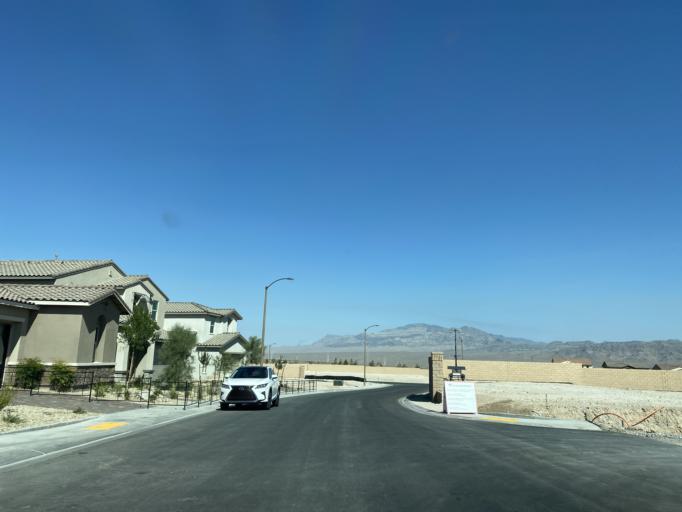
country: US
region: Nevada
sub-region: Clark County
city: Summerlin South
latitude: 36.3187
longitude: -115.3121
